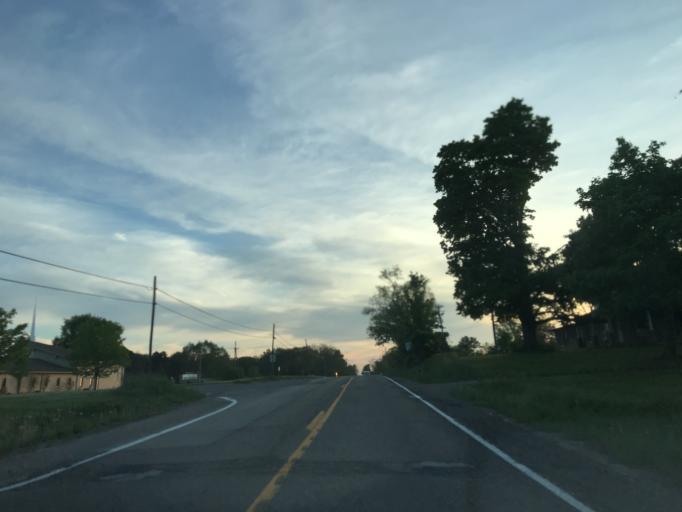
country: US
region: Michigan
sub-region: Oakland County
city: South Lyon
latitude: 42.4340
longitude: -83.5882
